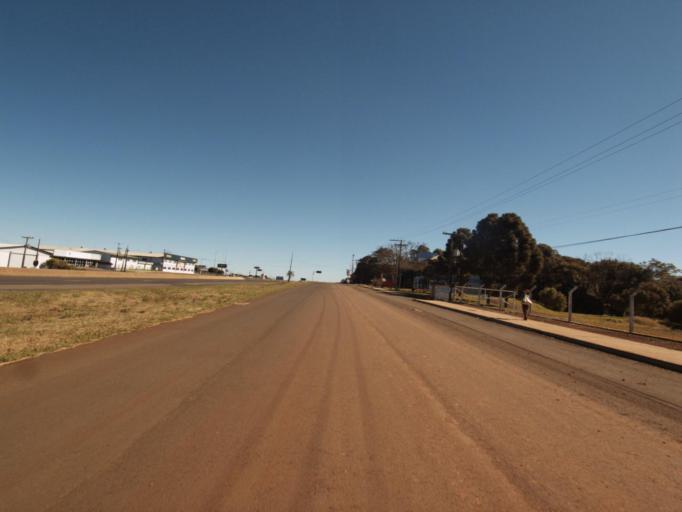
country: BR
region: Santa Catarina
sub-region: Xanxere
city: Xanxere
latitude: -26.8815
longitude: -52.3778
